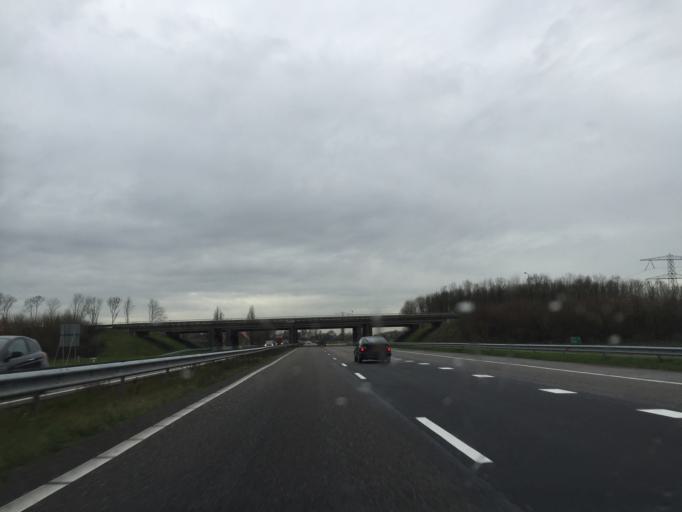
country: NL
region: North Brabant
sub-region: Gemeente Moerdijk
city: Klundert
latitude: 51.6221
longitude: 4.5155
